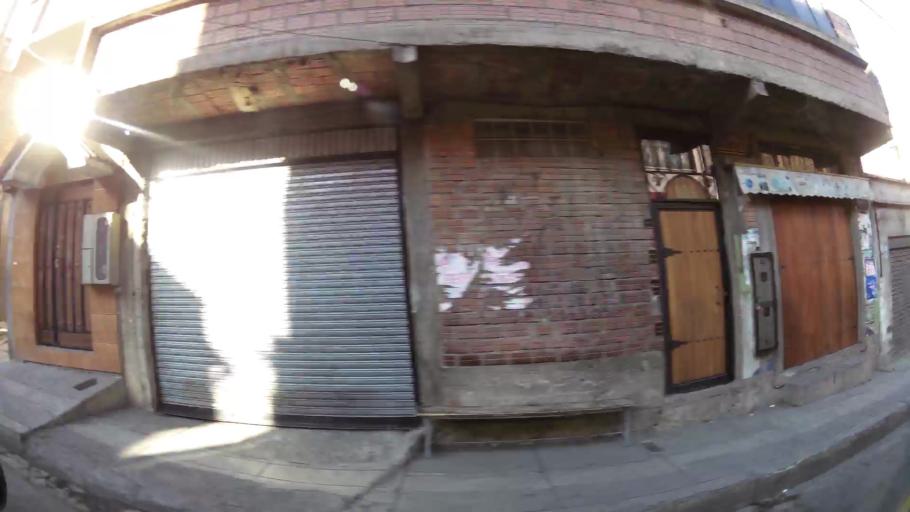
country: BO
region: La Paz
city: La Paz
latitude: -16.5021
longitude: -68.1528
